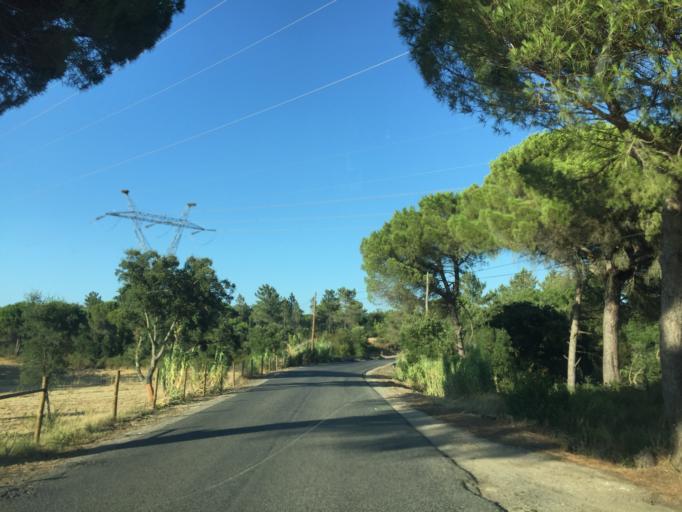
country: PT
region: Lisbon
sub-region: Azambuja
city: Aveiras de Cima
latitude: 39.1115
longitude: -8.9583
